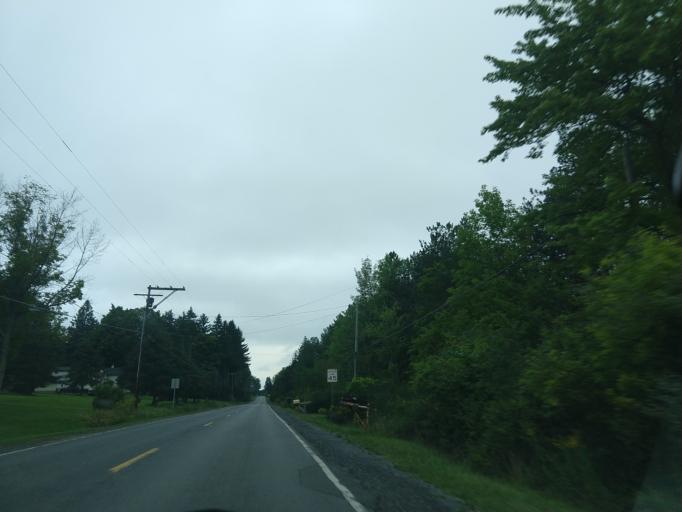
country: US
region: New York
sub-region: Tompkins County
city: South Hill
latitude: 42.4123
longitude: -76.4743
